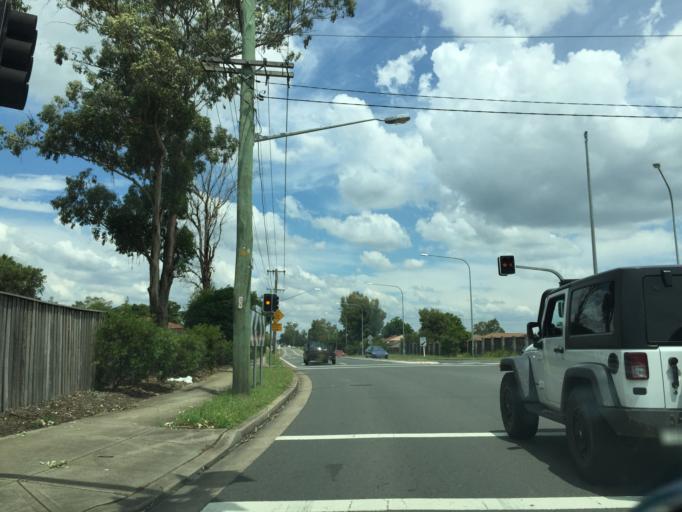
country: AU
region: New South Wales
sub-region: Blacktown
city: Hassall Grove
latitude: -33.7377
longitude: 150.8442
